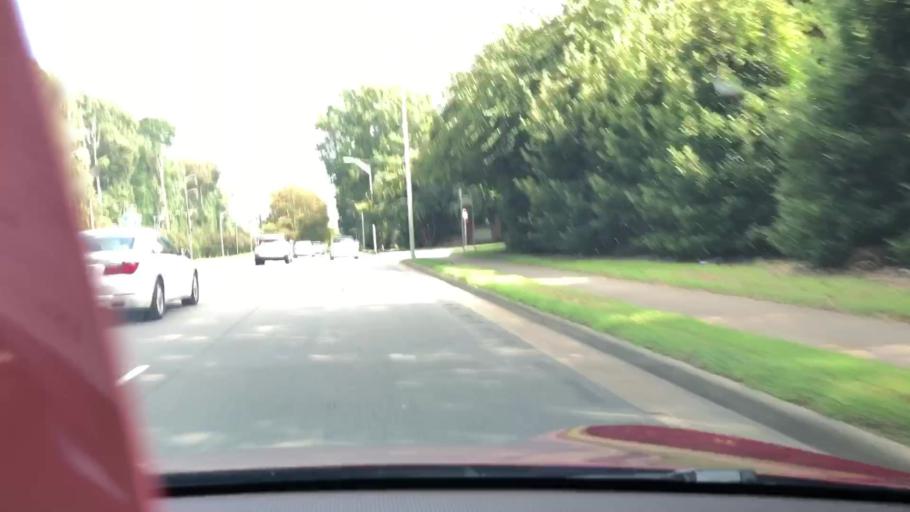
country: US
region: Virginia
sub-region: City of Virginia Beach
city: Virginia Beach
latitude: 36.8920
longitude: -76.0557
